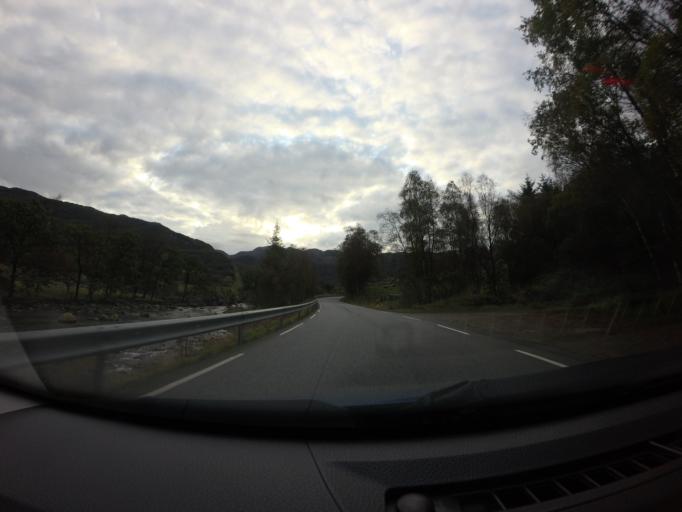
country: NO
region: Rogaland
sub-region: Forsand
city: Forsand
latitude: 58.8023
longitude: 6.2611
